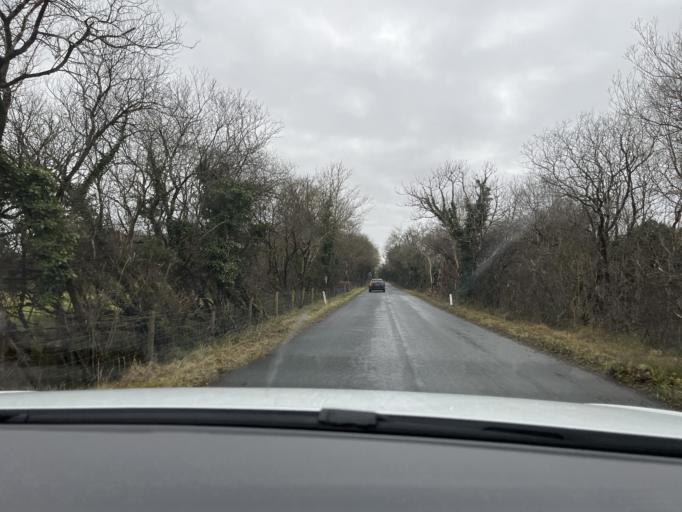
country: IE
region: Connaught
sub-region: County Leitrim
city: Manorhamilton
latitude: 54.2642
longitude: -8.2312
